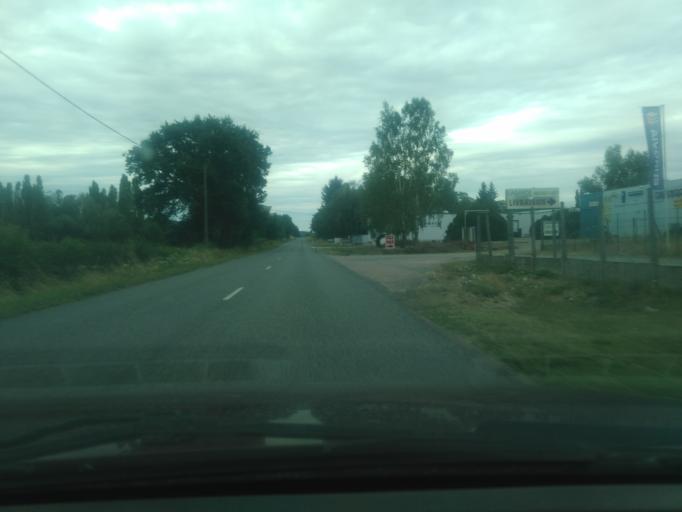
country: FR
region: Bourgogne
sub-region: Departement de la Nievre
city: Decize
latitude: 46.8045
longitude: 3.4462
